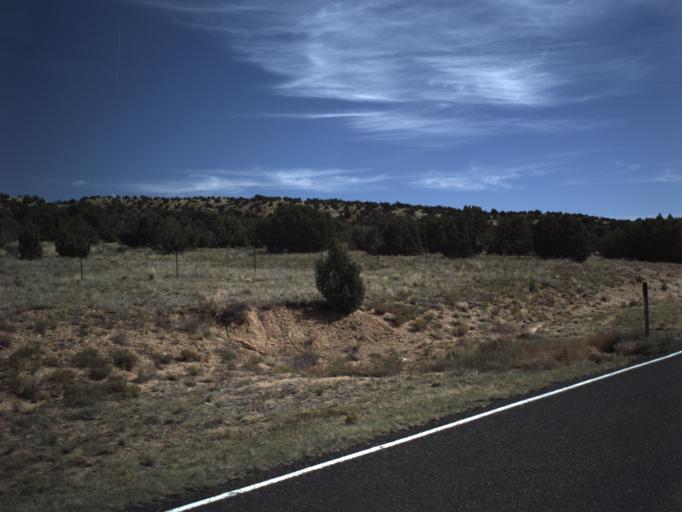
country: US
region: Utah
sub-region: Wayne County
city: Loa
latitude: 37.7388
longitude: -111.5499
